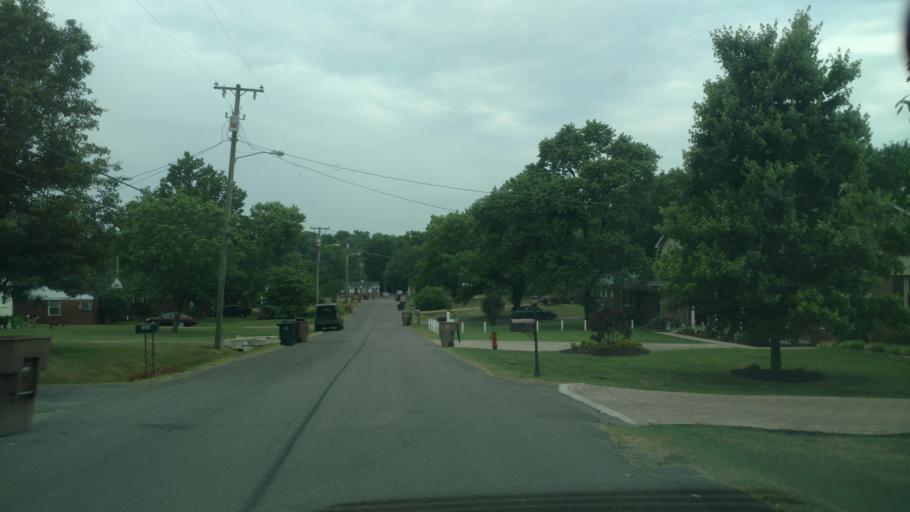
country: US
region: Tennessee
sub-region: Davidson County
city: Lakewood
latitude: 36.2031
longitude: -86.7053
